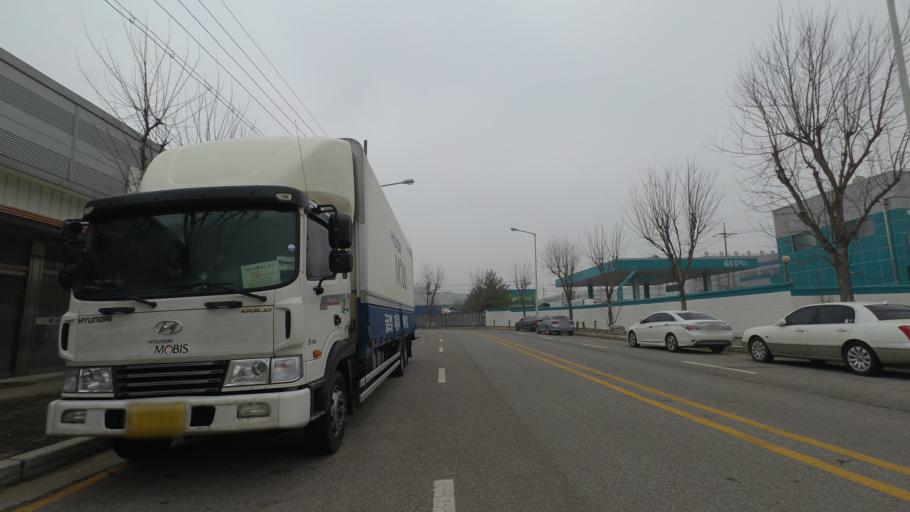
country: KR
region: Chungcheongnam-do
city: Tangjin
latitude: 36.9742
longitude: 126.8441
